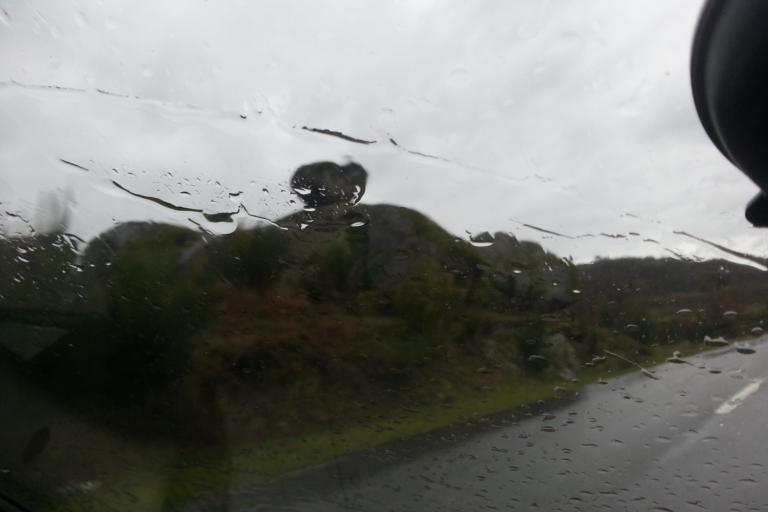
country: PT
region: Guarda
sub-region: Fornos de Algodres
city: Fornos de Algodres
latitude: 40.5774
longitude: -7.5107
